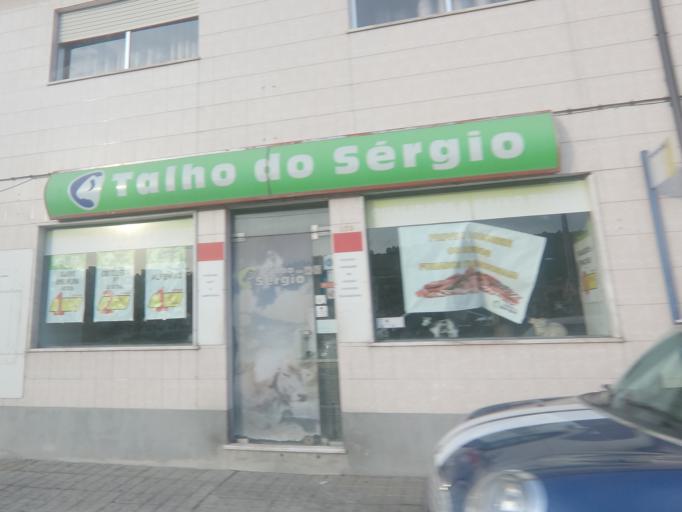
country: PT
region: Porto
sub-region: Valongo
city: Valongo
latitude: 41.1873
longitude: -8.4889
